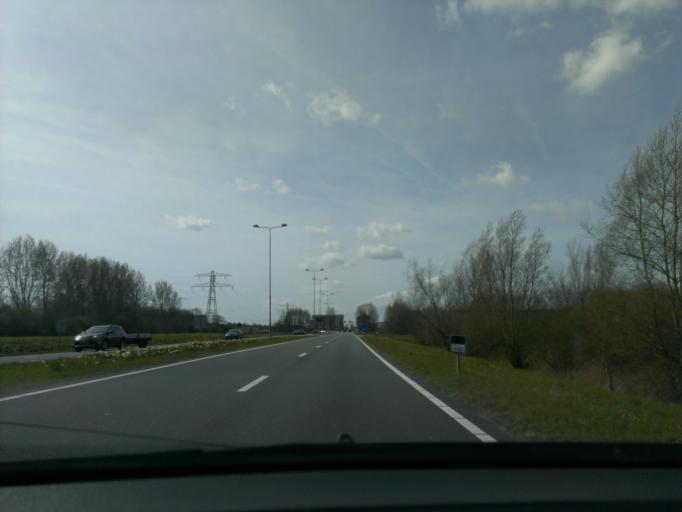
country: NL
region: North Holland
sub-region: Gemeente Haarlemmermeer
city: Hoofddorp
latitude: 52.3265
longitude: 4.6623
